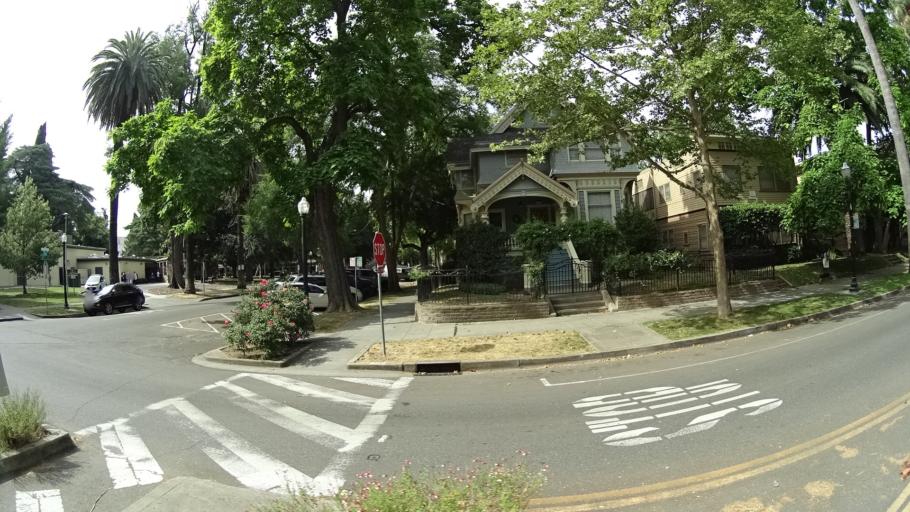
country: US
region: California
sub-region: Sacramento County
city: Sacramento
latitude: 38.5753
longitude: -121.4703
